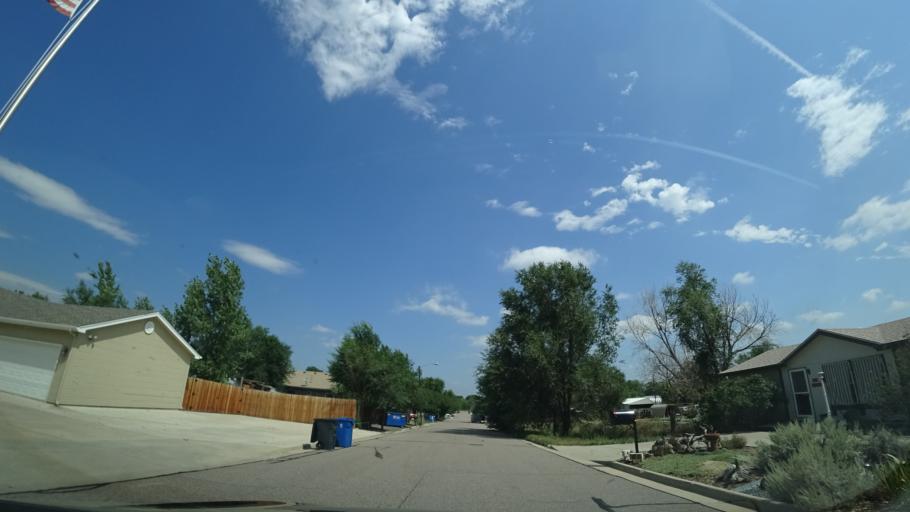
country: US
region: Colorado
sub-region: Jefferson County
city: Lakewood
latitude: 39.7153
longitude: -105.0686
